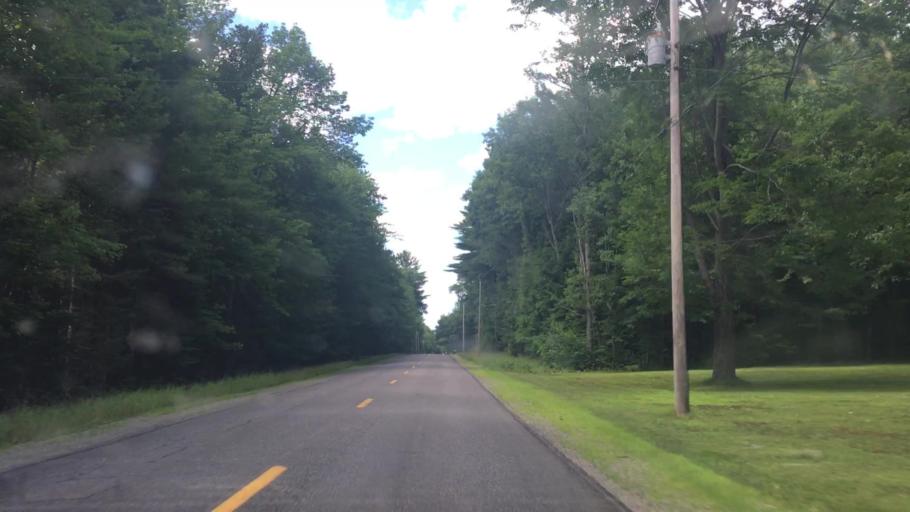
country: US
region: Maine
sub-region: Franklin County
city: Chesterville
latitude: 44.6035
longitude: -70.0838
